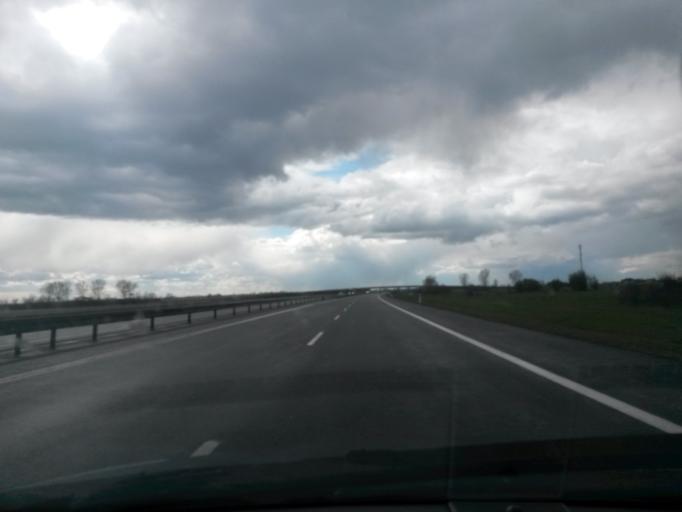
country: PL
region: Greater Poland Voivodeship
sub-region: Powiat poznanski
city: Kleszczewo
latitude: 52.3081
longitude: 17.1945
